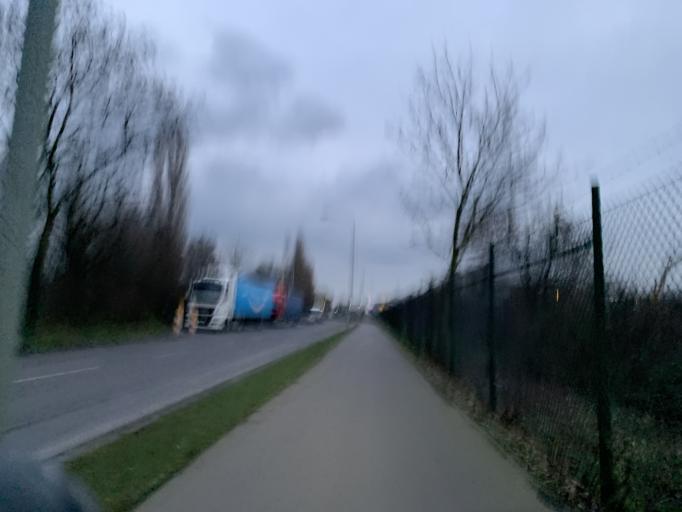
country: DE
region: North Rhine-Westphalia
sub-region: Regierungsbezirk Dusseldorf
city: Meerbusch
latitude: 51.3369
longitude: 6.6873
